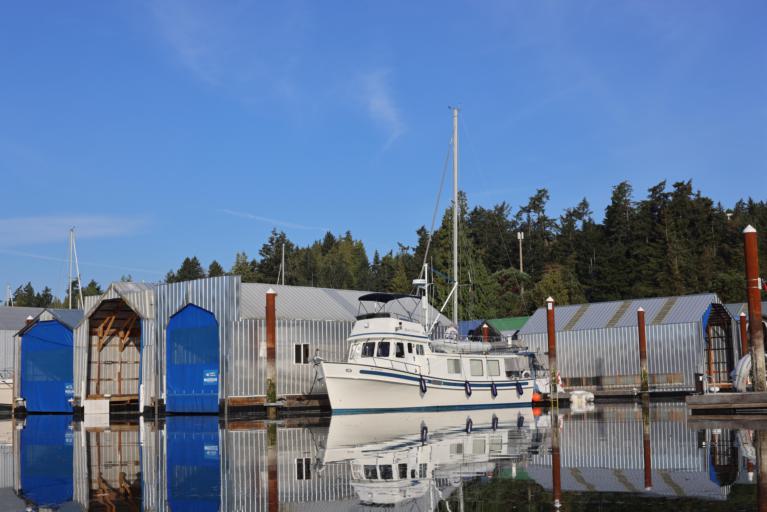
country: CA
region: British Columbia
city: North Saanich
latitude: 48.6798
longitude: -123.4151
